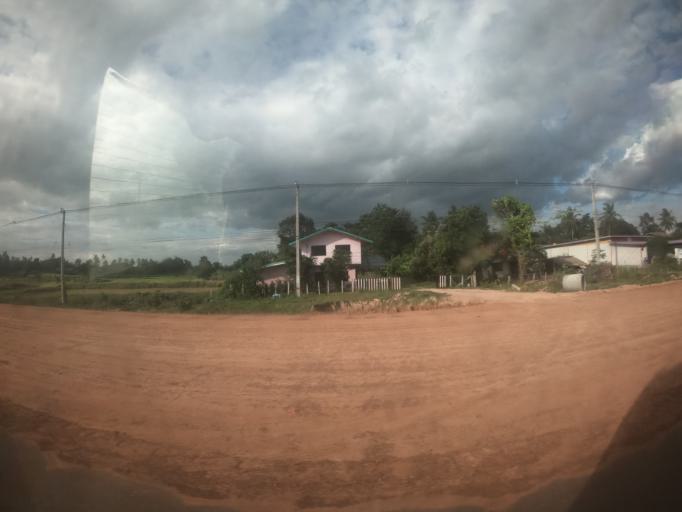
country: TH
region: Surin
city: Kap Choeng
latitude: 14.4984
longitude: 103.5658
